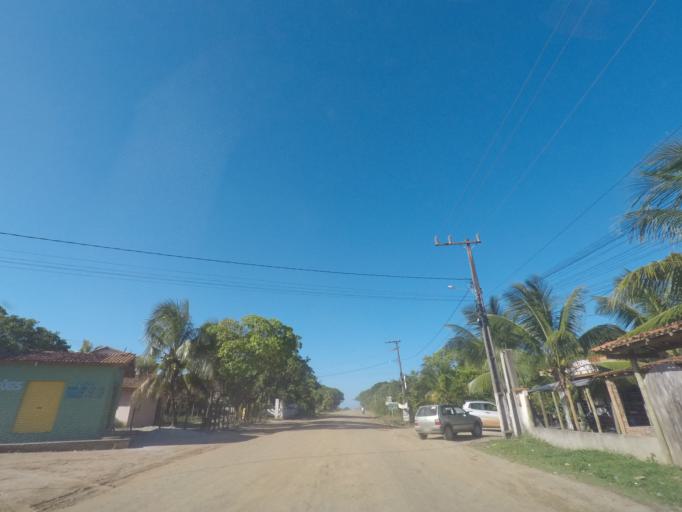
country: BR
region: Bahia
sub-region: Marau
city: Marau
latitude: -14.0398
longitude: -38.9554
